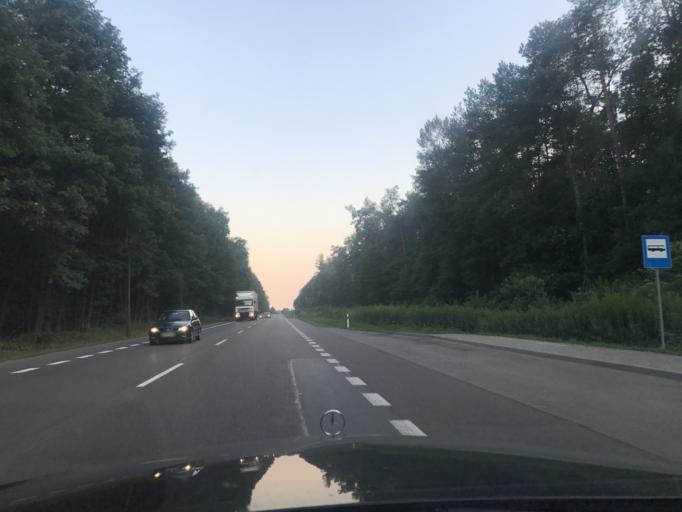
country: PL
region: Lublin Voivodeship
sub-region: Powiat lubelski
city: Niemce
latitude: 51.3824
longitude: 22.6351
